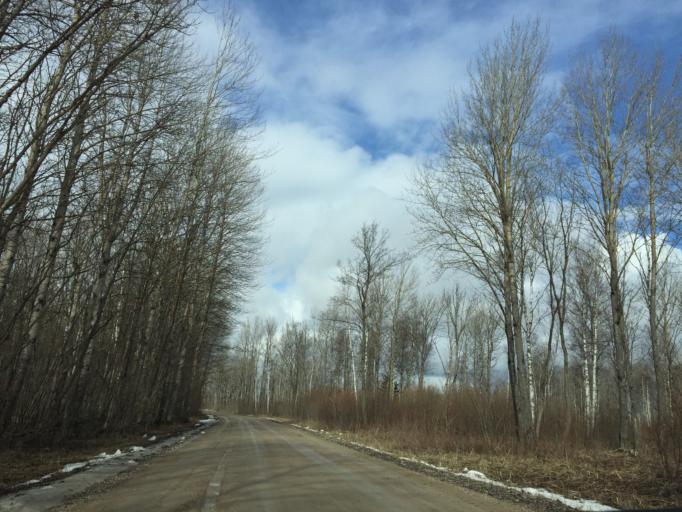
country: EE
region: Laeaene
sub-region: Lihula vald
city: Lihula
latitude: 58.7308
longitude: 23.8313
